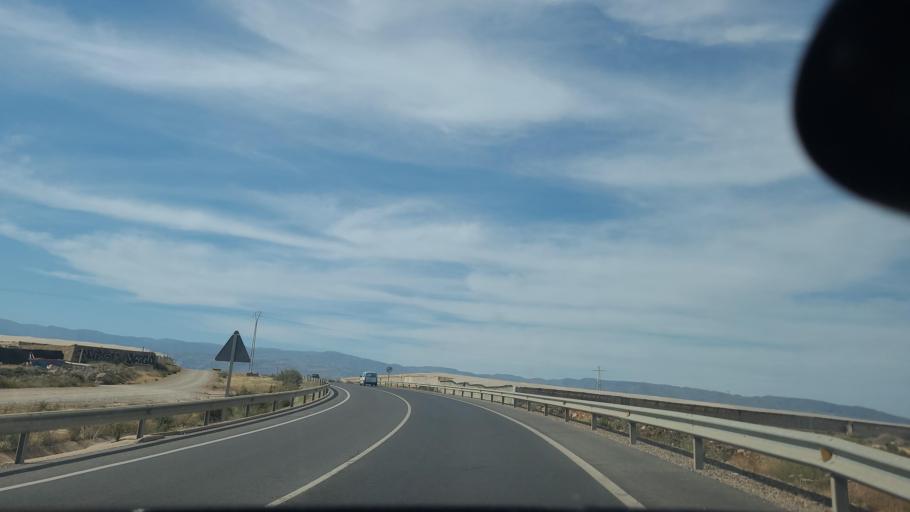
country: ES
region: Andalusia
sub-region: Provincia de Almeria
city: Roquetas de Mar
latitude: 36.7378
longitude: -2.6241
